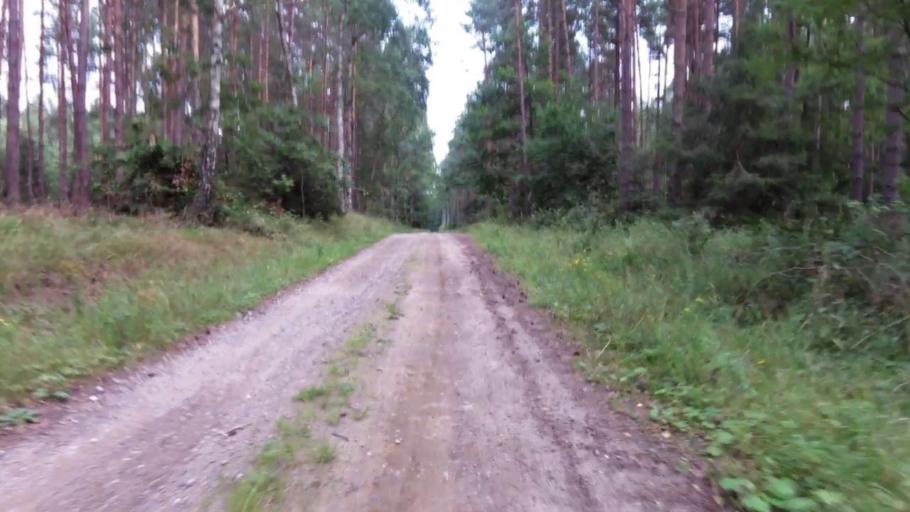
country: PL
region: West Pomeranian Voivodeship
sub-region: Powiat drawski
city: Drawsko Pomorskie
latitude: 53.5629
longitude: 15.8775
